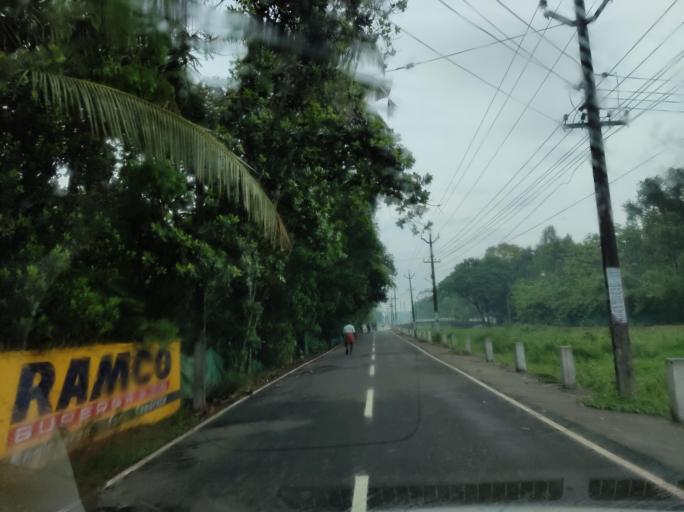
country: IN
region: Kerala
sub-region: Alappuzha
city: Alleppey
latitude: 9.5613
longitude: 76.3300
